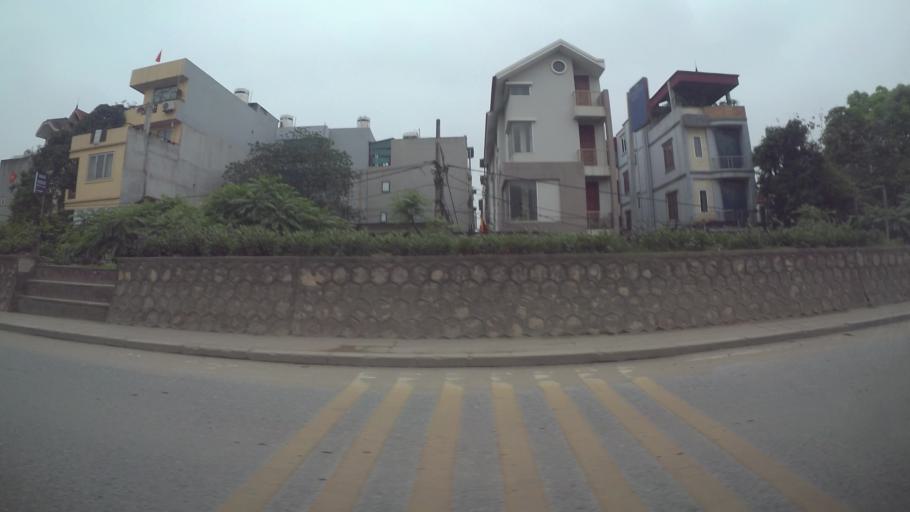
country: VN
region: Ha Noi
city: Hai BaTrung
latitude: 20.9937
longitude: 105.8925
